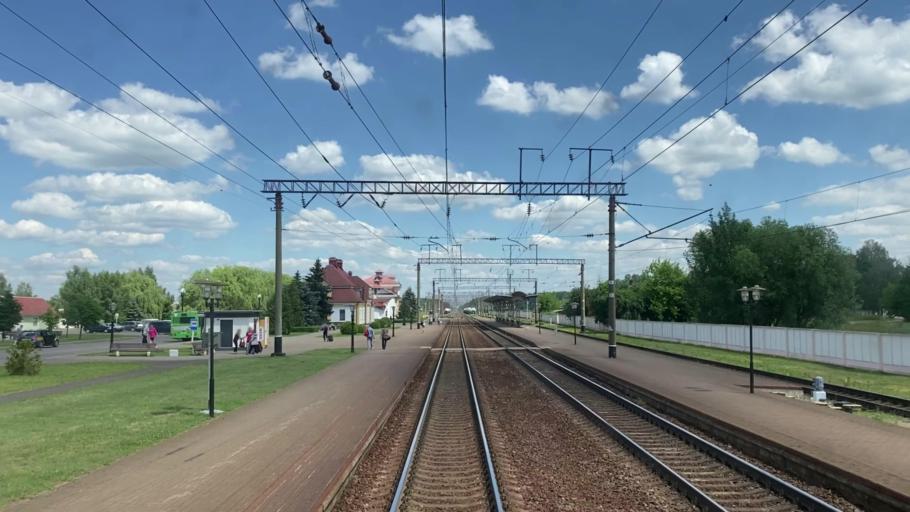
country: BY
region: Brest
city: Pruzhany
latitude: 52.4698
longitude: 24.5209
